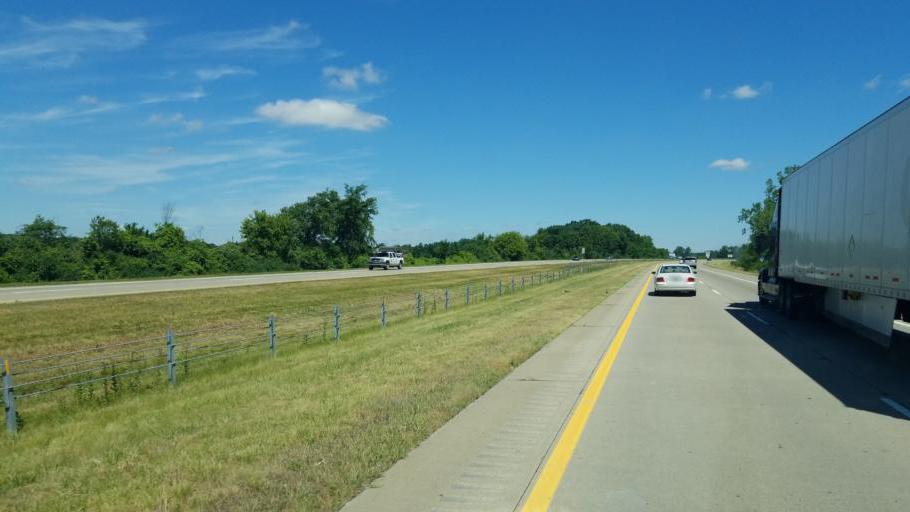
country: US
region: Ohio
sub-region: Lucas County
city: Sylvania
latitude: 41.7356
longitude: -83.6913
